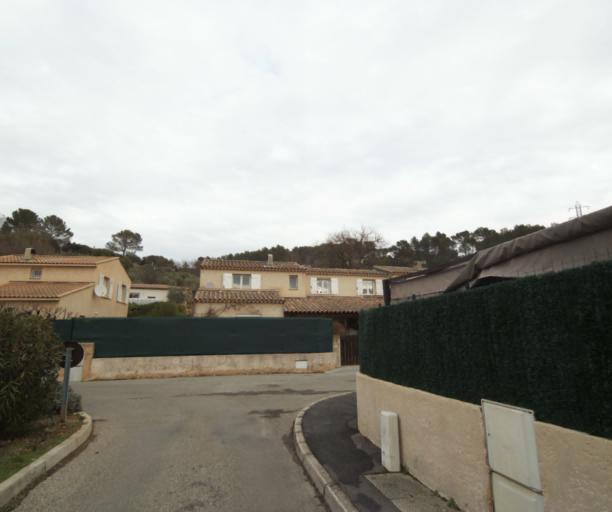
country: FR
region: Provence-Alpes-Cote d'Azur
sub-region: Departement du Var
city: Trans-en-Provence
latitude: 43.5087
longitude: 6.4837
